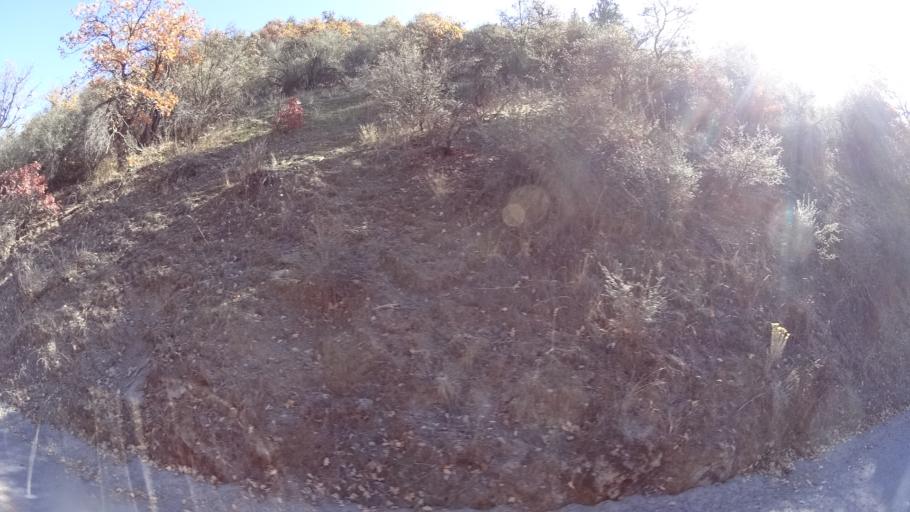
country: US
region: California
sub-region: Siskiyou County
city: Yreka
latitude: 41.8287
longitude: -122.6559
